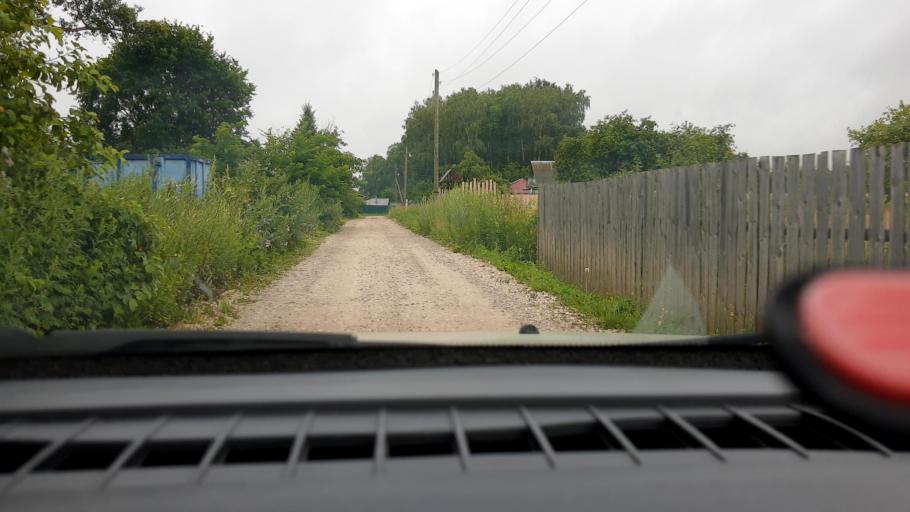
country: RU
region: Vladimir
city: Luknovo
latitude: 56.2242
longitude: 42.0240
